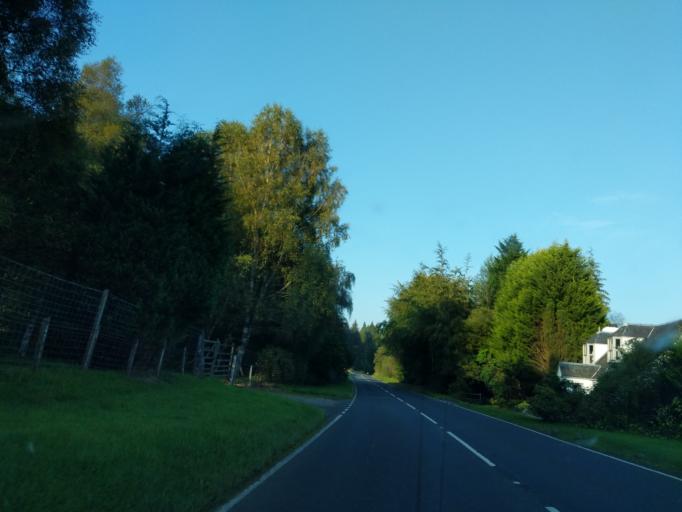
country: GB
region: Scotland
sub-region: Stirling
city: Balfron
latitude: 56.1755
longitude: -4.3312
